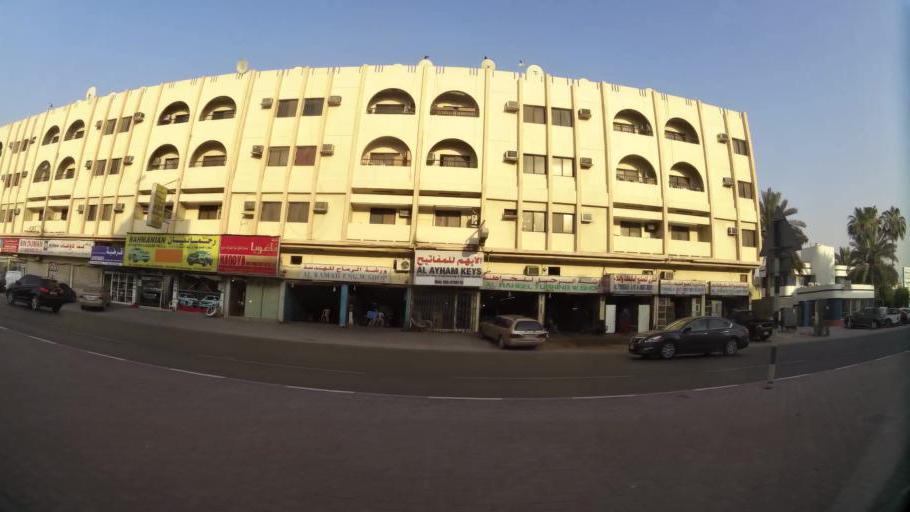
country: AE
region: Ash Shariqah
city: Sharjah
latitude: 25.3328
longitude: 55.4112
